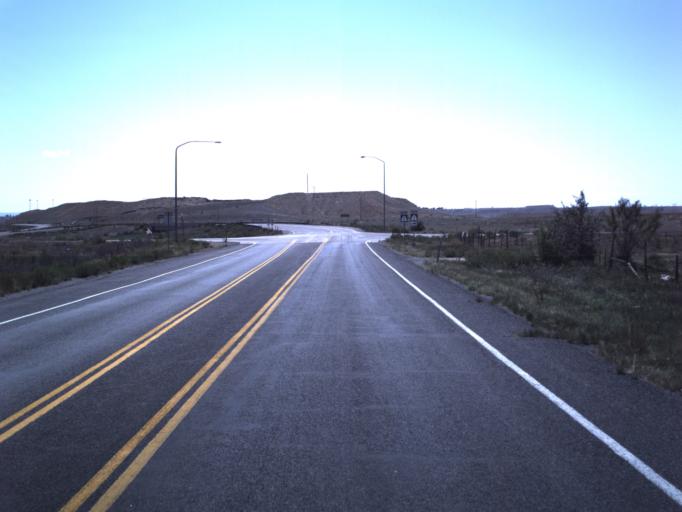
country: US
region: Utah
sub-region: Emery County
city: Castle Dale
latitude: 39.1795
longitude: -111.0476
